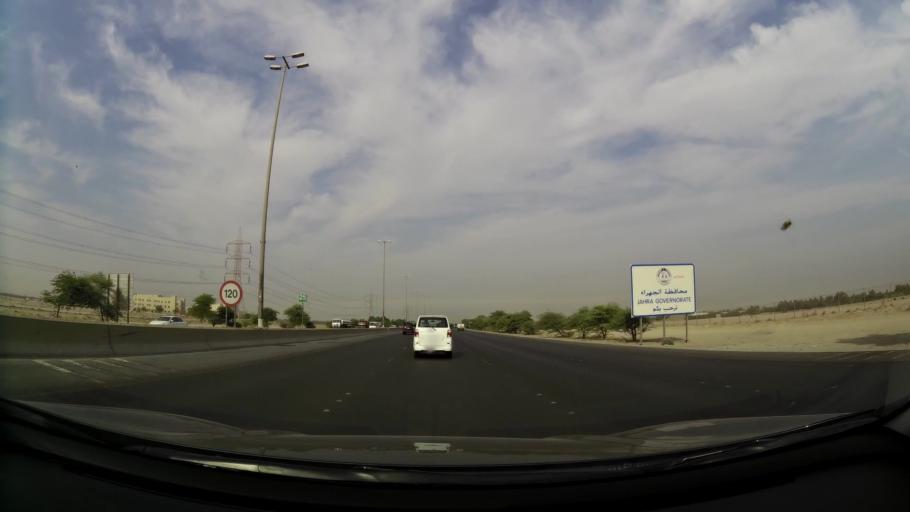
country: KW
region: Al Asimah
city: Ar Rabiyah
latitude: 29.2676
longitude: 47.8288
